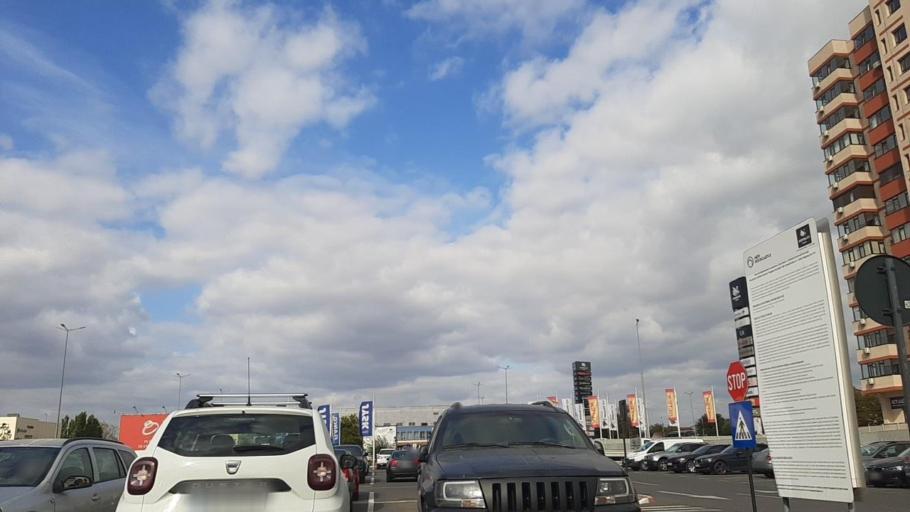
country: RO
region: Galati
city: Galati
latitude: 45.4518
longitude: 28.0336
